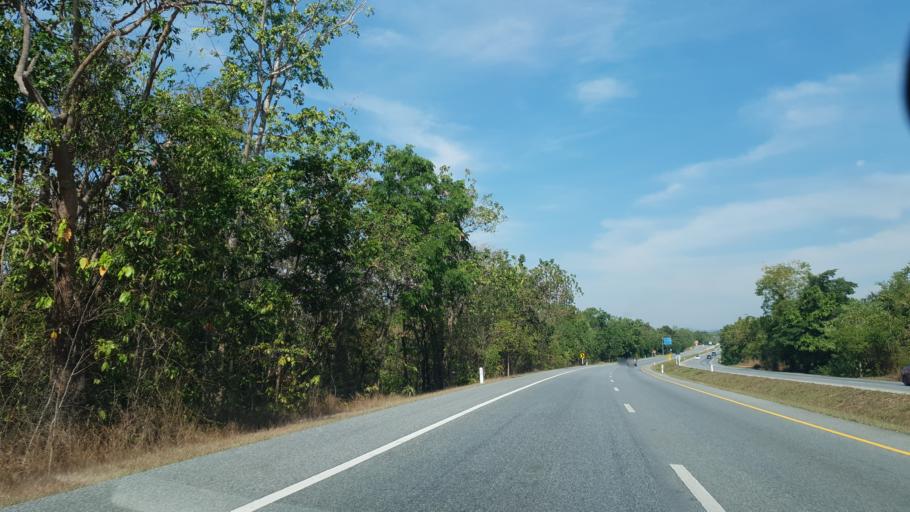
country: TH
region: Uttaradit
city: Thong Saen Khan
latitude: 17.4271
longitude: 100.2260
